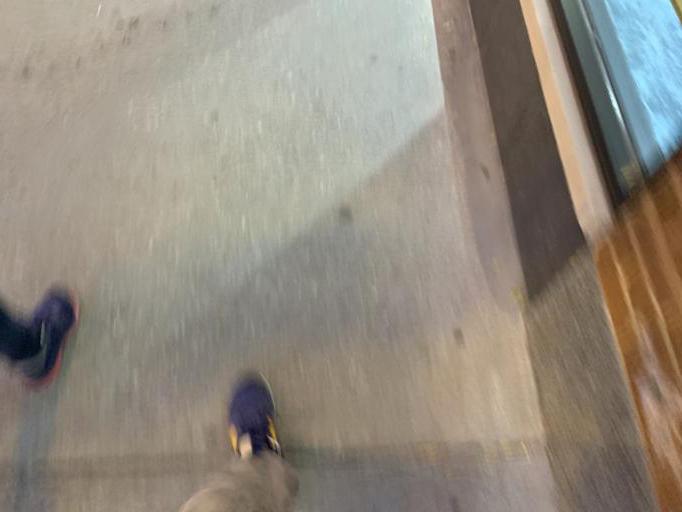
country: US
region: Illinois
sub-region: Cook County
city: Lincolnwood
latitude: 41.9651
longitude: -87.6863
